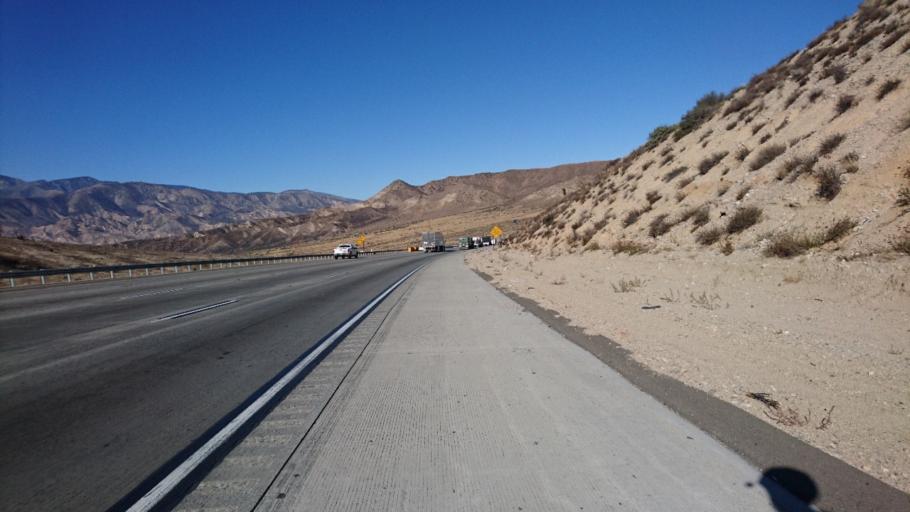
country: US
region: California
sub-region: San Bernardino County
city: Oak Hills
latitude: 34.3449
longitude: -117.4637
